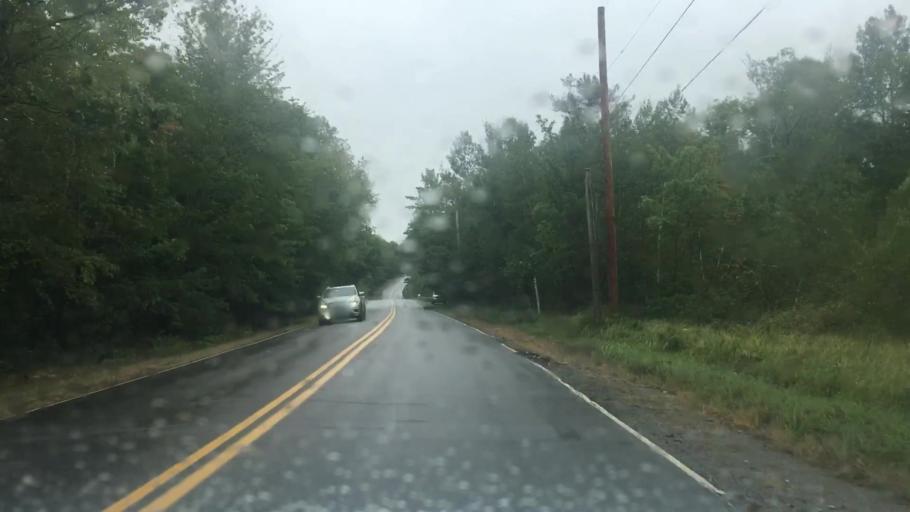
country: US
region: Maine
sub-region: Penobscot County
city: Hudson
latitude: 44.9860
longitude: -68.7951
